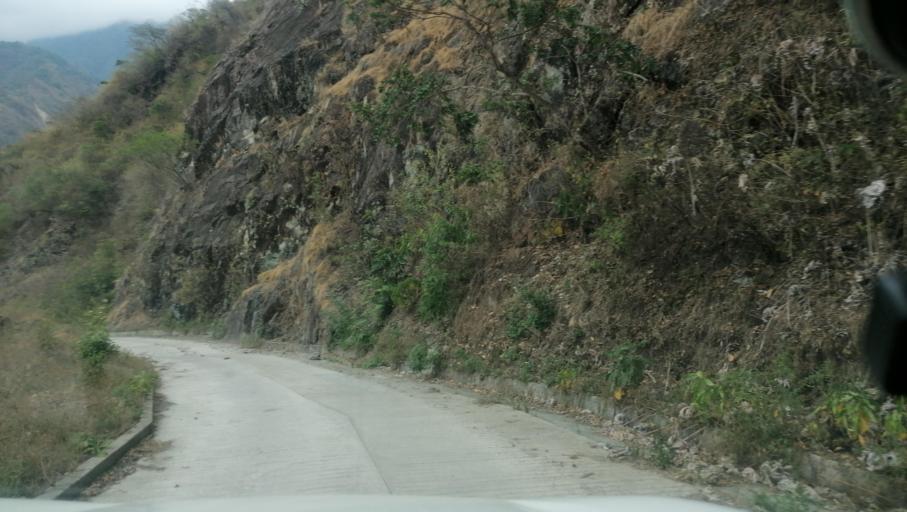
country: MX
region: Chiapas
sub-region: Cacahoatan
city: Benito Juarez
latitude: 15.1617
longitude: -92.1756
